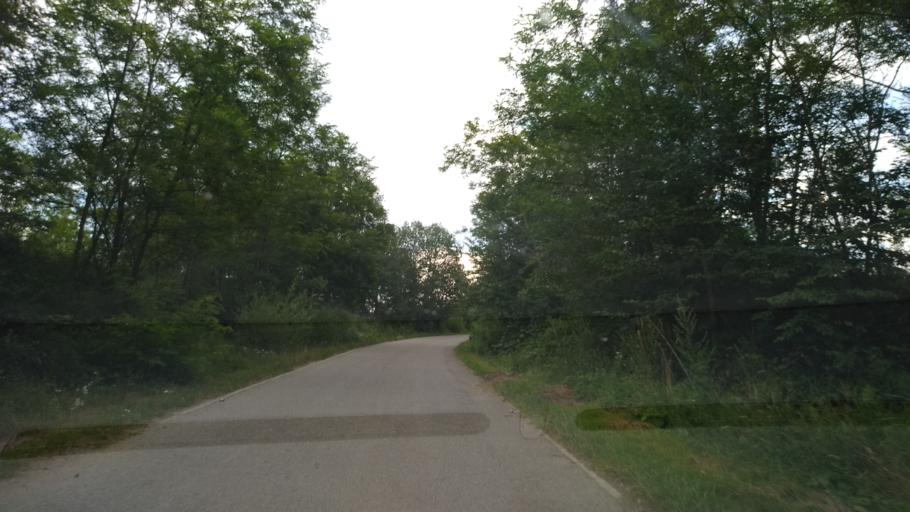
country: RO
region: Hunedoara
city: Salasu de Sus
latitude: 45.5058
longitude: 22.9590
